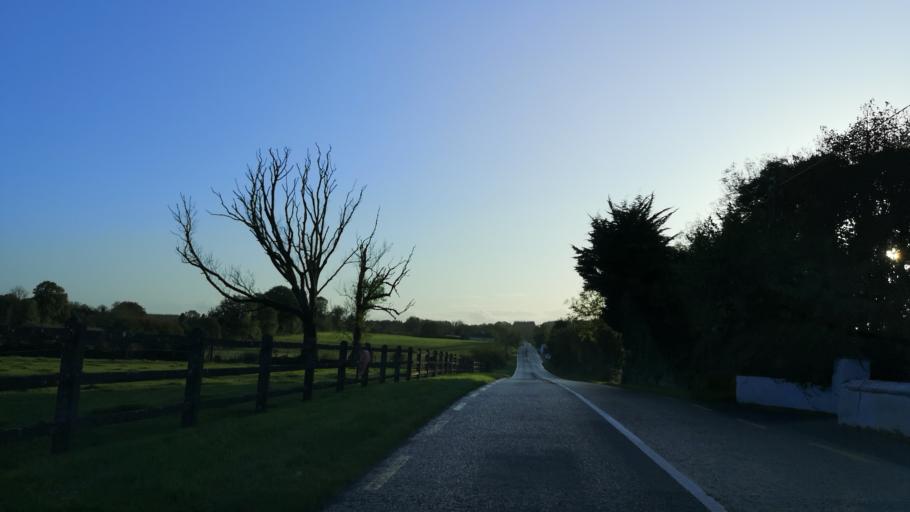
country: IE
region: Connaught
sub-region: Roscommon
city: Castlerea
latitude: 53.7457
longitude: -8.5380
